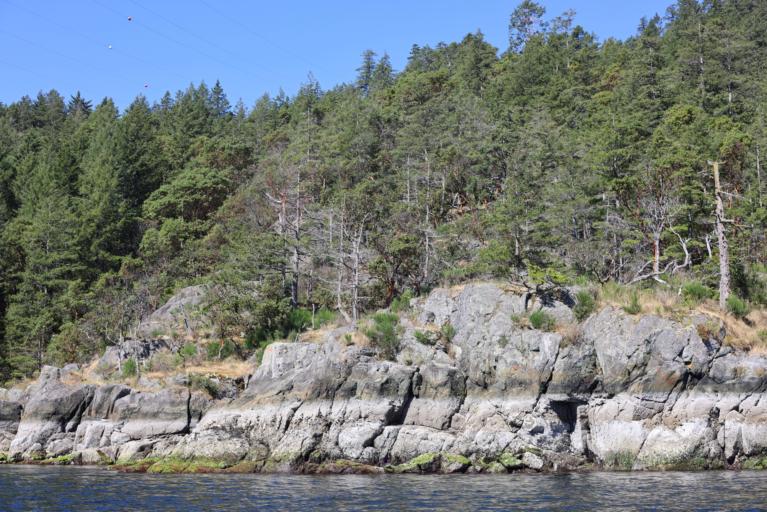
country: CA
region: British Columbia
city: North Cowichan
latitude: 48.8282
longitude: -123.5844
